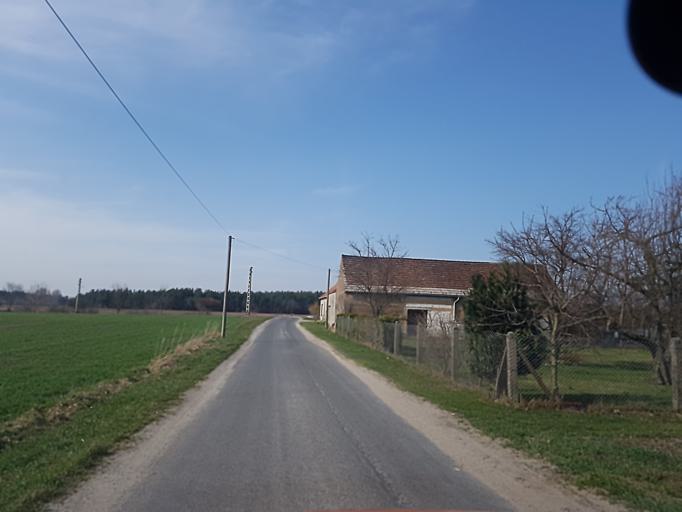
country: DE
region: Brandenburg
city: Bronkow
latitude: 51.6415
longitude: 13.8668
